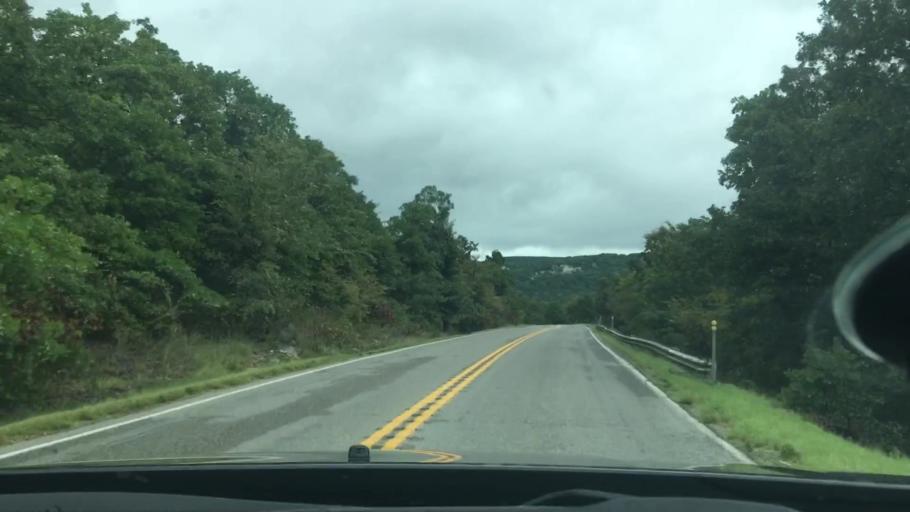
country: US
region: Oklahoma
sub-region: Sequoyah County
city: Vian
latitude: 35.6290
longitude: -94.9648
